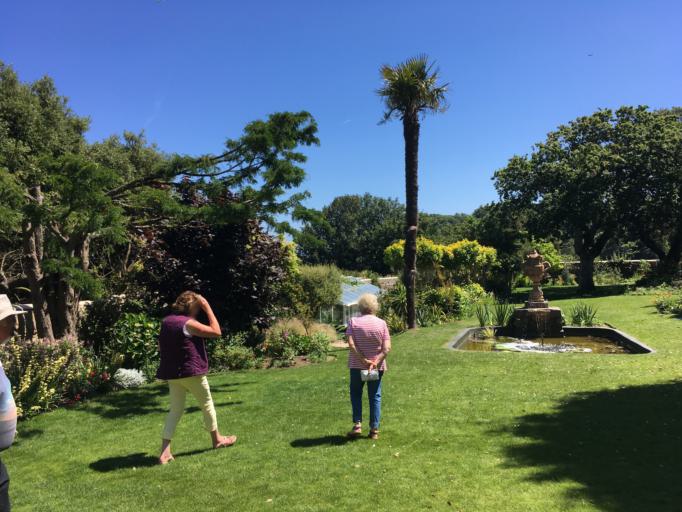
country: GG
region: St Peter Port
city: Saint Peter Port
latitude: 49.4512
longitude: -2.5375
